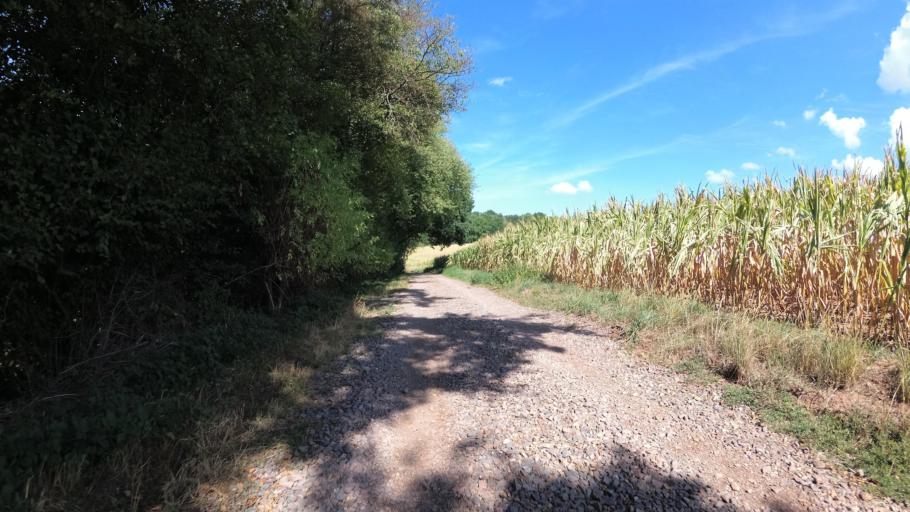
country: DE
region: Saarland
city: Mainzweiler
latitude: 49.4108
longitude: 7.0856
